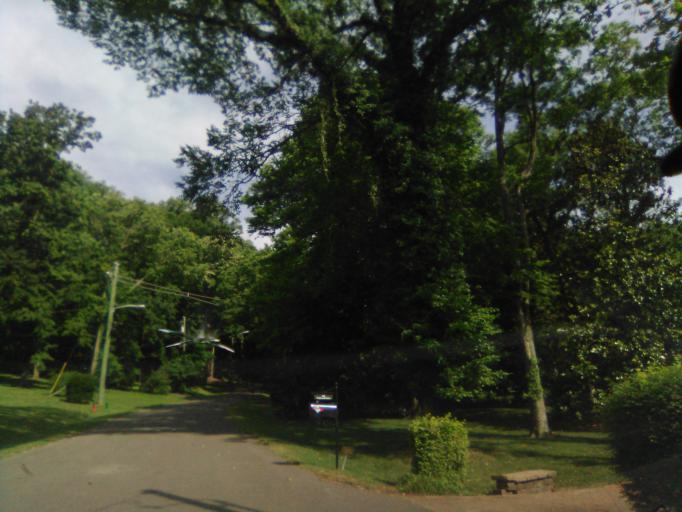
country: US
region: Tennessee
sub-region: Davidson County
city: Belle Meade
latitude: 36.1050
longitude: -86.8986
